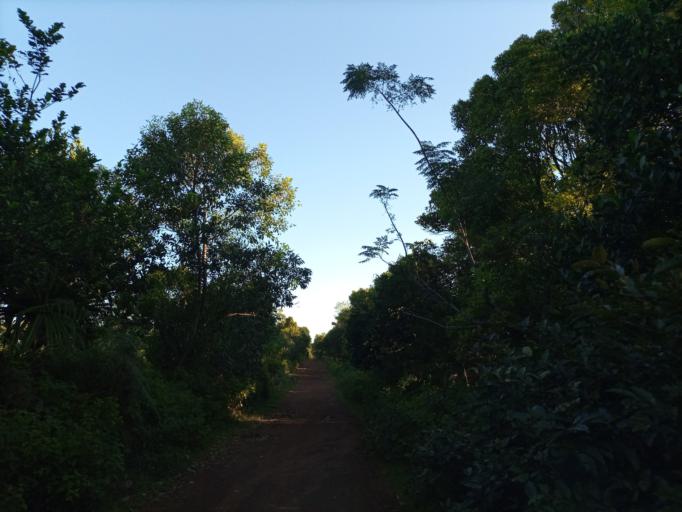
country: MG
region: Atsimo-Atsinanana
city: Vohipaho
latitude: -23.5260
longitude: 47.6189
